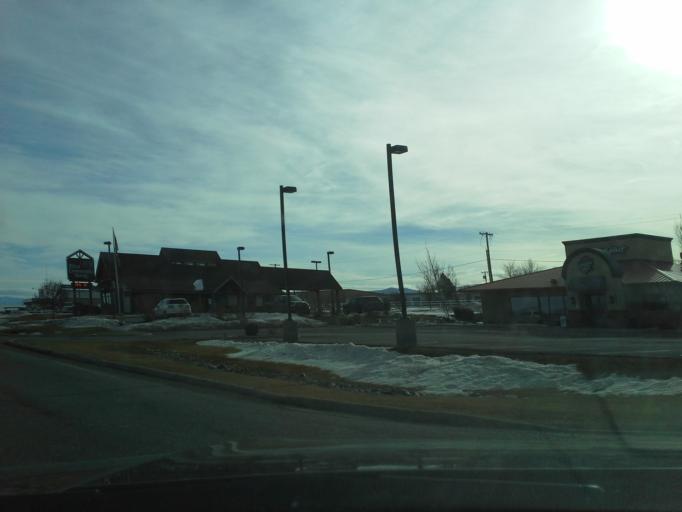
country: US
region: Montana
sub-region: Lewis and Clark County
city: Helena
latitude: 46.5910
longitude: -111.9887
